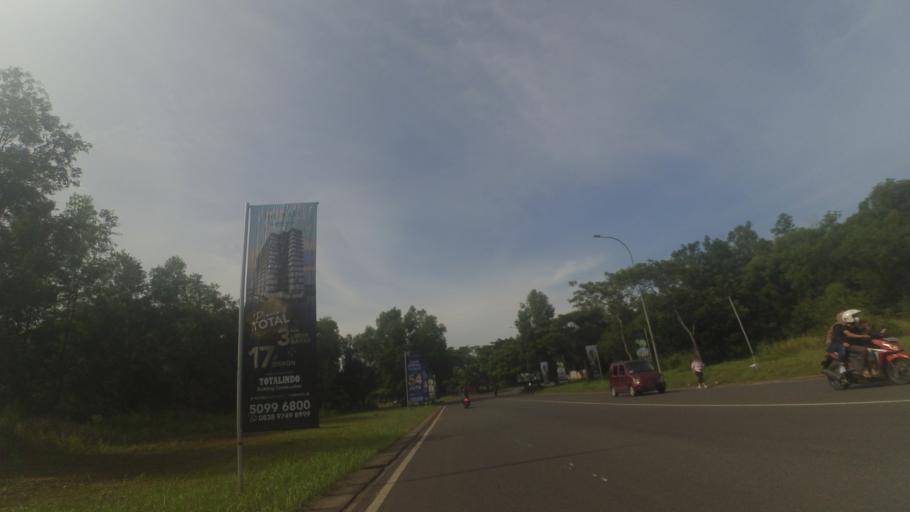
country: ID
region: West Java
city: Pamulang
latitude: -6.3451
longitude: 106.7727
